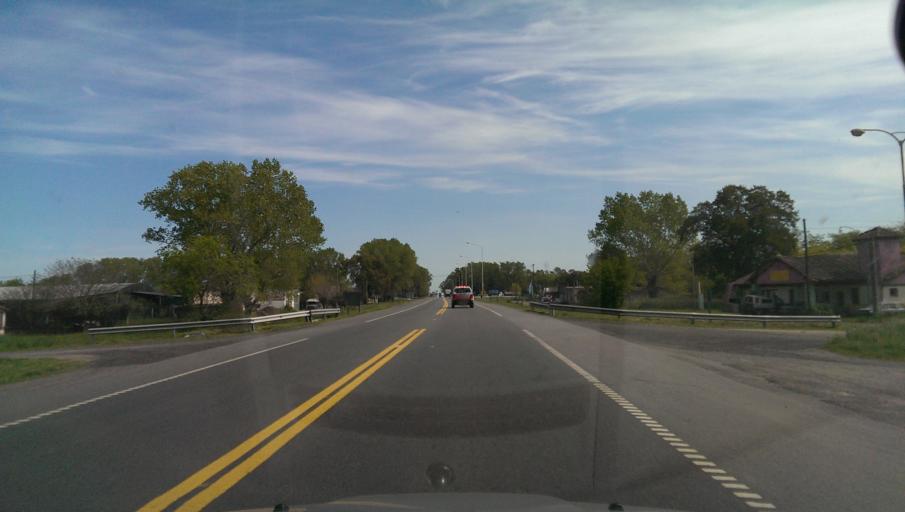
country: AR
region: Buenos Aires
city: Tapalque
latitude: -36.3851
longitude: -59.4895
